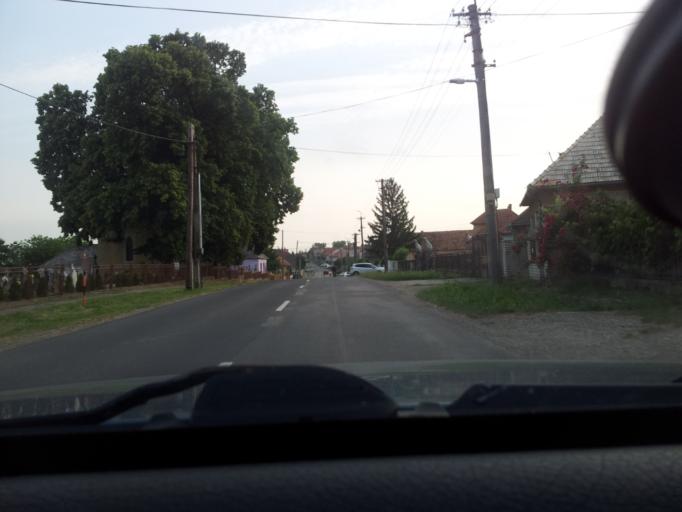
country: SK
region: Nitriansky
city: Levice
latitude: 48.2855
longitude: 18.6525
